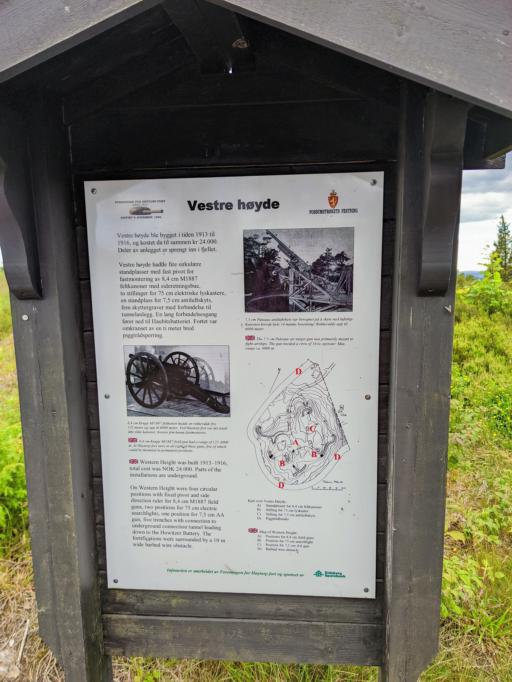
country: NO
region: Ostfold
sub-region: Eidsberg
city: Mysen
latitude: 59.5600
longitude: 11.3412
